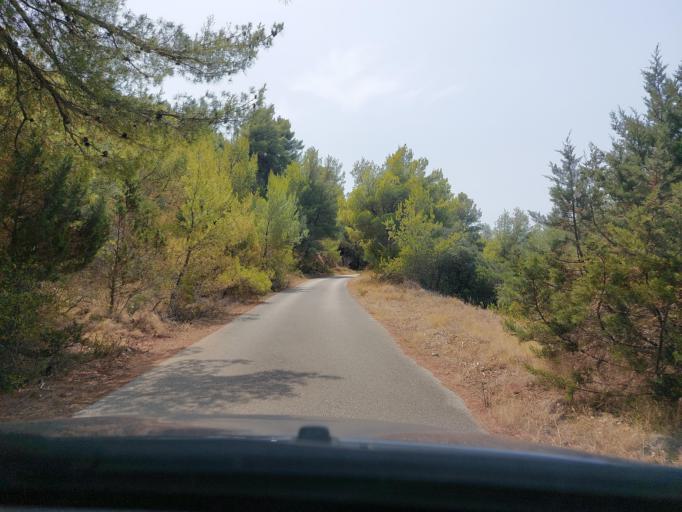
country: HR
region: Dubrovacko-Neretvanska
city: Smokvica
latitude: 42.7294
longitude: 16.8899
